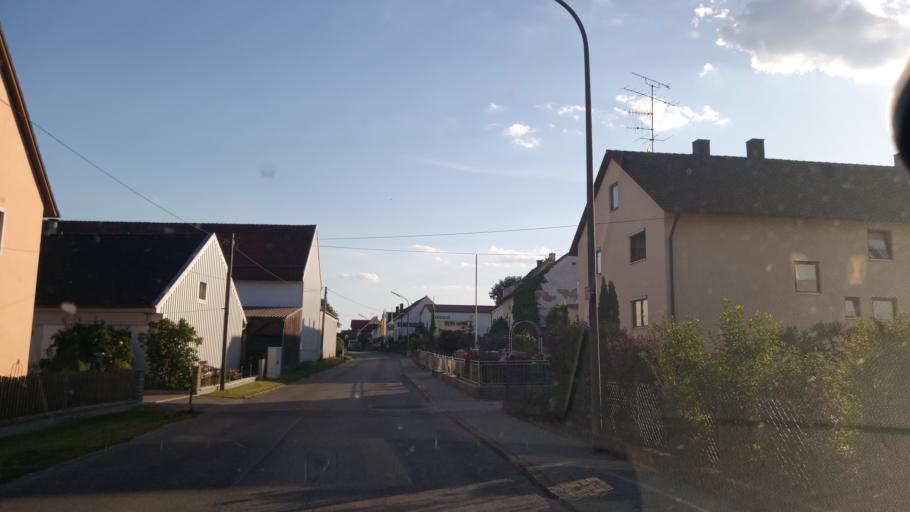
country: DE
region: Bavaria
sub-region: Upper Bavaria
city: Markt Indersdorf
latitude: 48.3699
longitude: 11.3865
